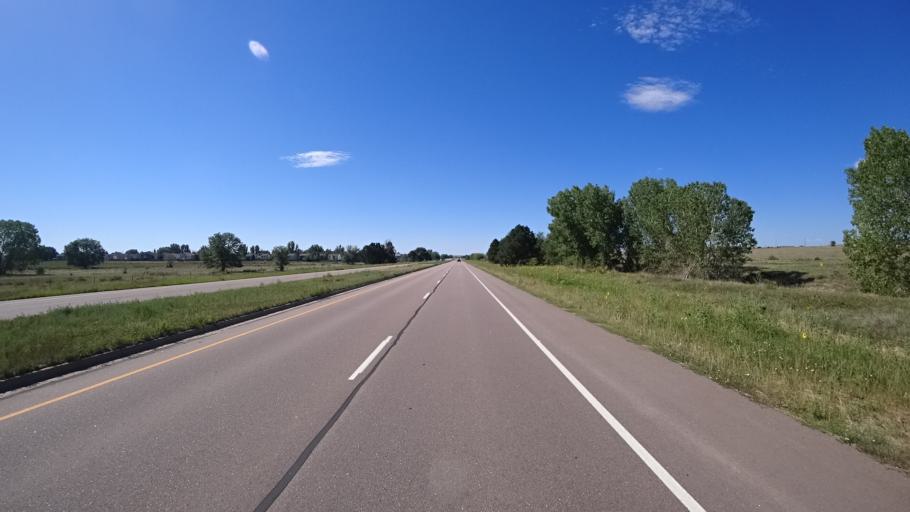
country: US
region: Colorado
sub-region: El Paso County
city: Security-Widefield
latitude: 38.7716
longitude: -104.6598
